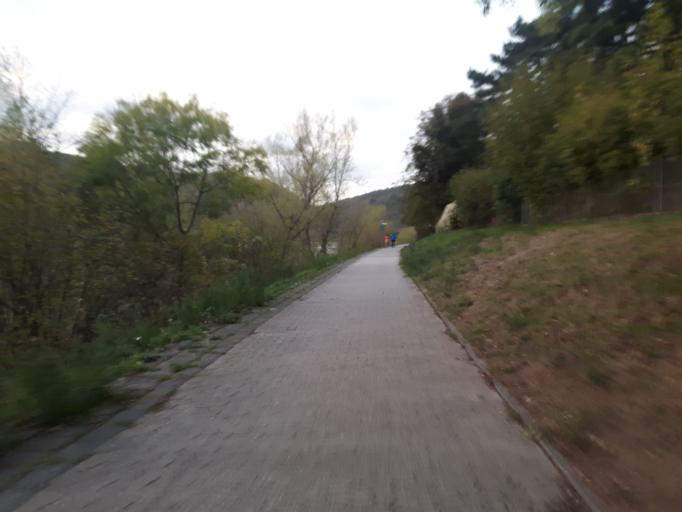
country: DE
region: Rheinland-Pfalz
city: Unkel
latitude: 50.5912
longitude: 7.2143
